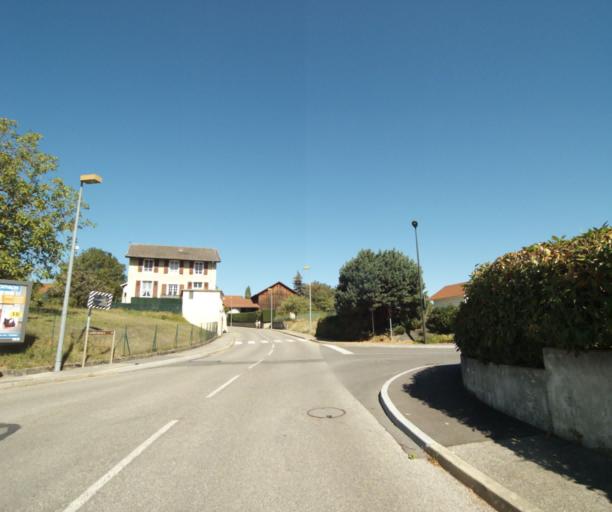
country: FR
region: Rhone-Alpes
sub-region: Departement de l'Ain
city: Ornex
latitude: 46.2635
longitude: 6.0939
